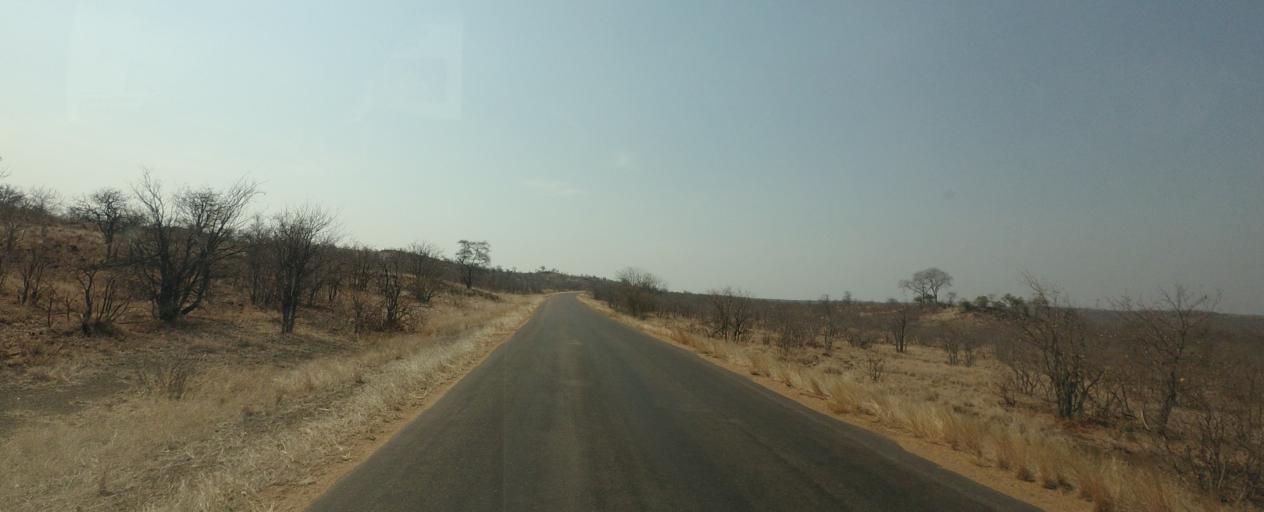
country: ZA
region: Limpopo
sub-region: Mopani District Municipality
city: Phalaborwa
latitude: -23.9926
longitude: 31.6428
